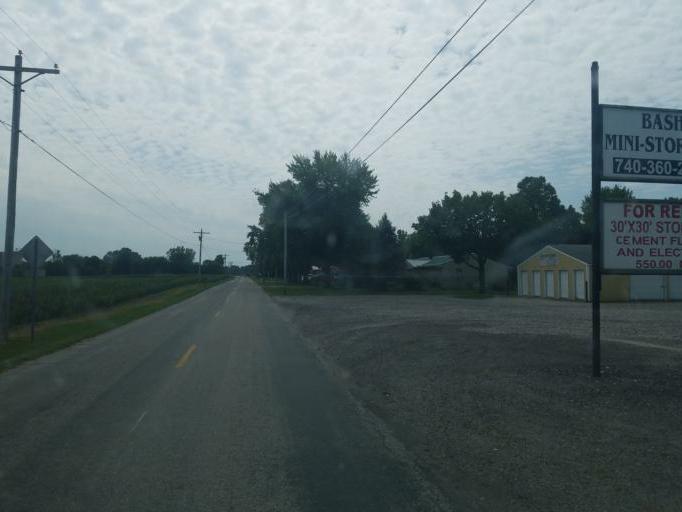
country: US
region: Ohio
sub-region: Marion County
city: Prospect
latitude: 40.5412
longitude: -83.2151
